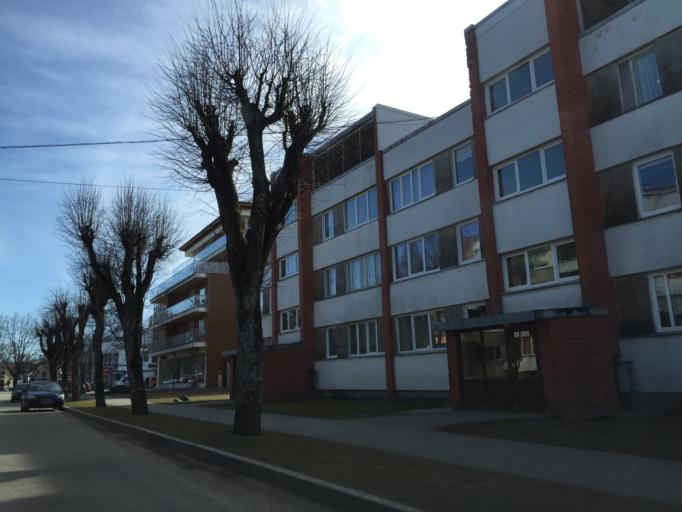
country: LV
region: Sigulda
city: Sigulda
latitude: 57.1581
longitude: 24.8491
